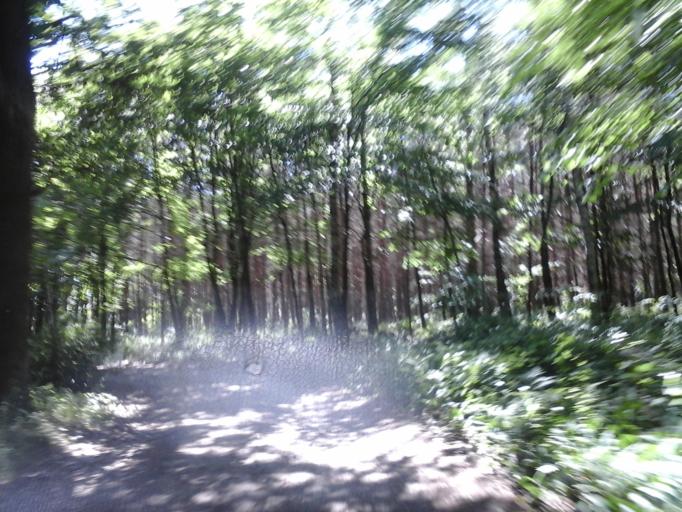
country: PL
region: Lubusz
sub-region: Powiat strzelecko-drezdenecki
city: Dobiegniew
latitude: 53.0929
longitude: 15.7792
